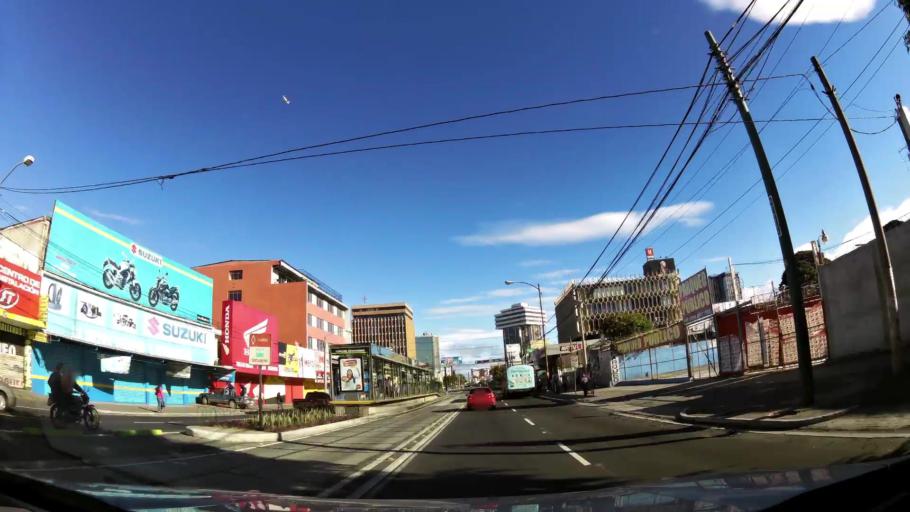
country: GT
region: Guatemala
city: Guatemala City
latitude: 14.6137
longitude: -90.5164
